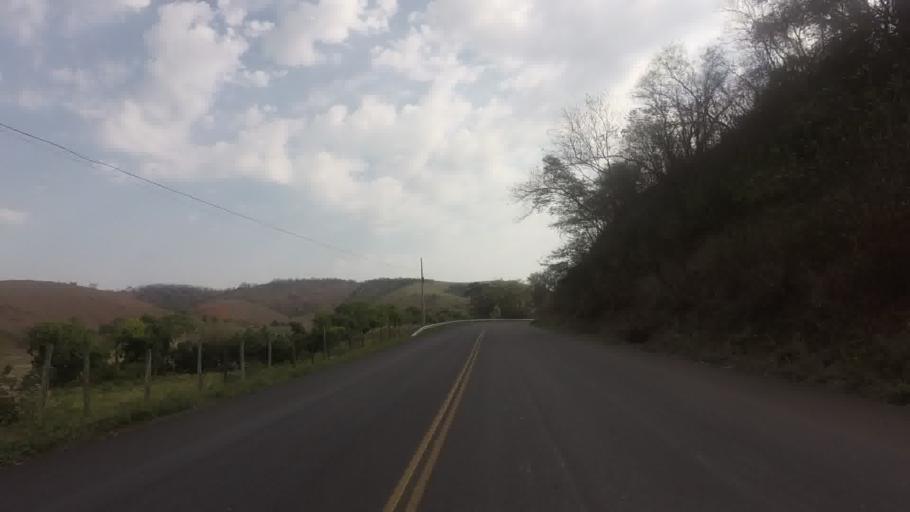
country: BR
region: Rio de Janeiro
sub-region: Itaperuna
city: Itaperuna
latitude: -21.3572
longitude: -41.9220
